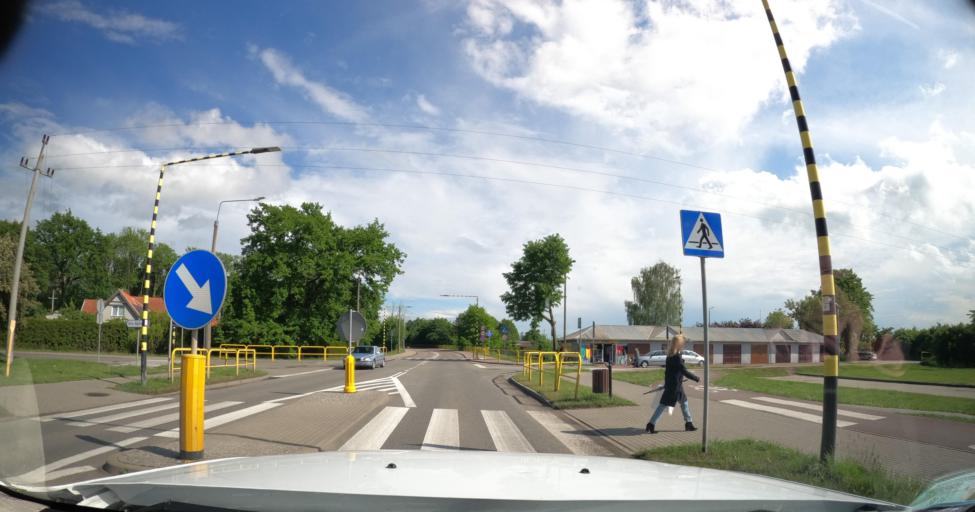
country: PL
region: Pomeranian Voivodeship
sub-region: Powiat nowodworski
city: Nowy Dwor Gdanski
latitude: 54.2092
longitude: 19.1124
